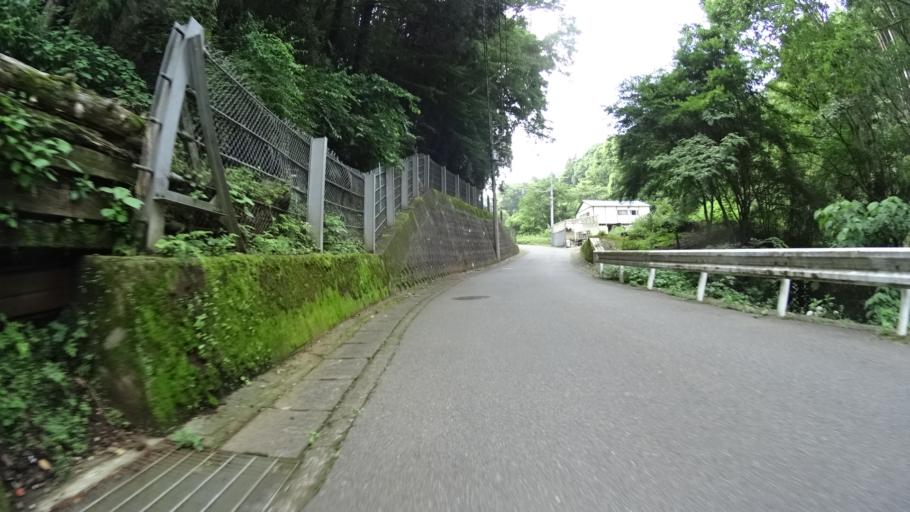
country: JP
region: Kanagawa
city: Atsugi
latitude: 35.4926
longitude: 139.2708
